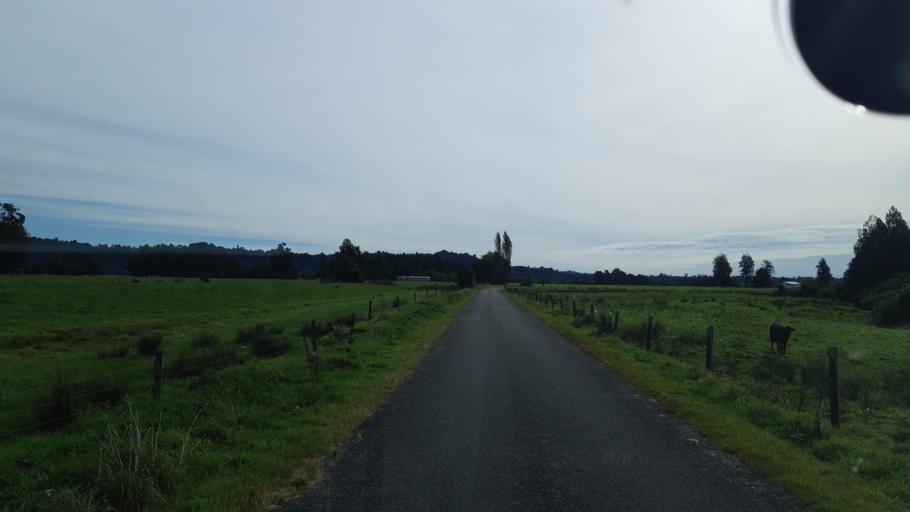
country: NZ
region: West Coast
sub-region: Westland District
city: Hokitika
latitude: -43.1281
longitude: 170.4998
